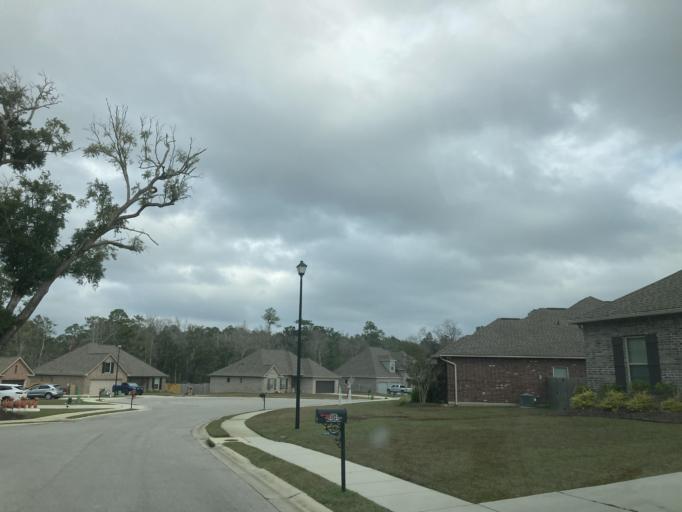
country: US
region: Mississippi
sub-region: Harrison County
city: D'Iberville
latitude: 30.4775
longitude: -88.9968
